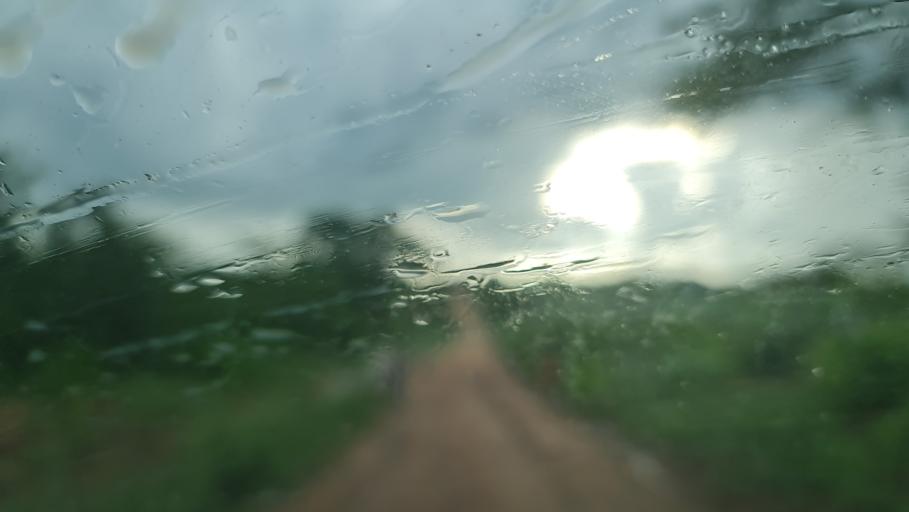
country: MZ
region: Nampula
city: Nacala
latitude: -13.9866
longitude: 40.3862
